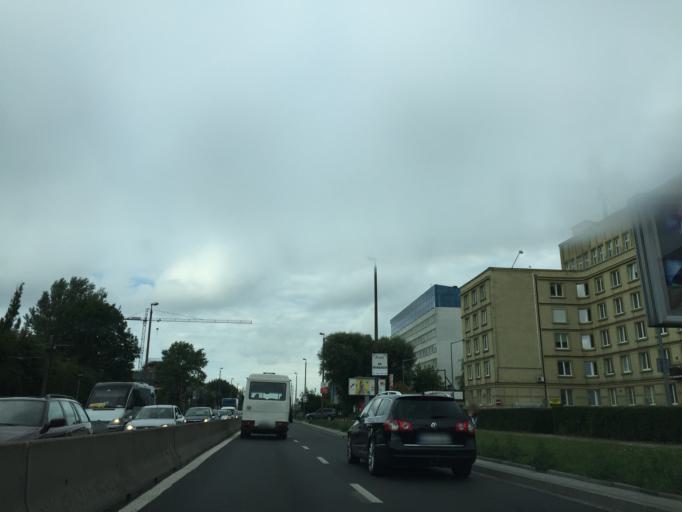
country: PL
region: Lesser Poland Voivodeship
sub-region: Krakow
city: Krakow
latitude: 50.0303
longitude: 19.9372
